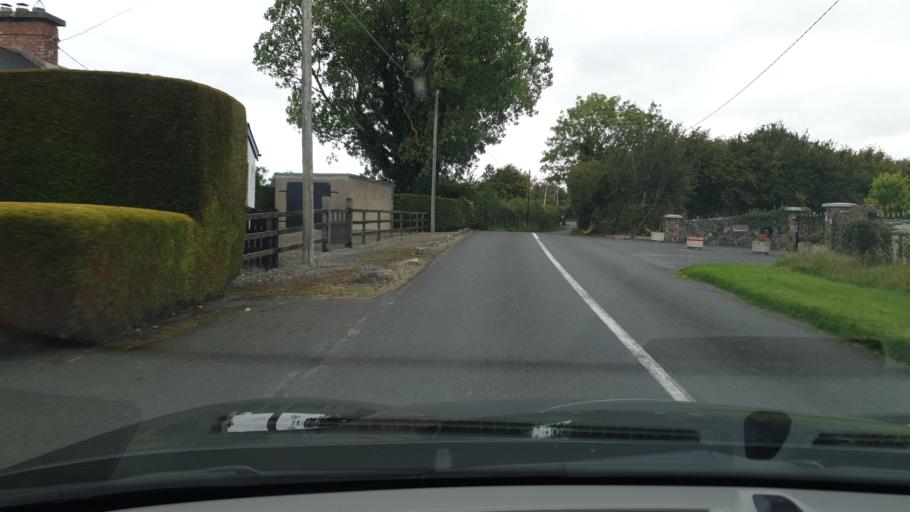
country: IE
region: Leinster
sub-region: Kildare
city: Clane
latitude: 53.3284
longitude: -6.6397
